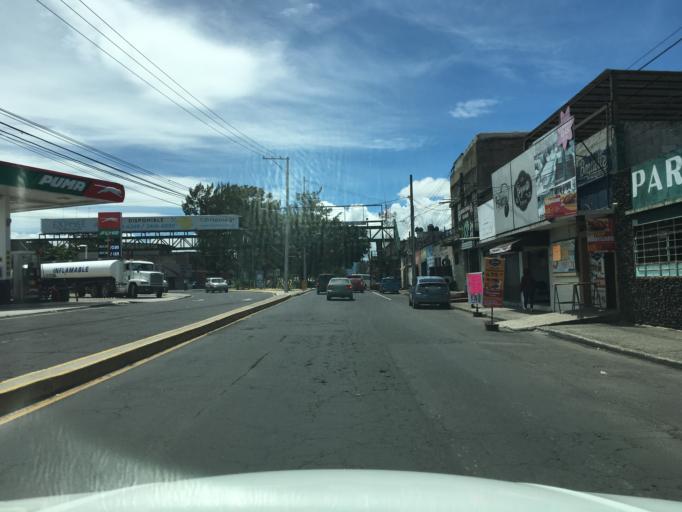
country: GT
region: Guatemala
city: Guatemala City
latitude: 14.6292
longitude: -90.5456
